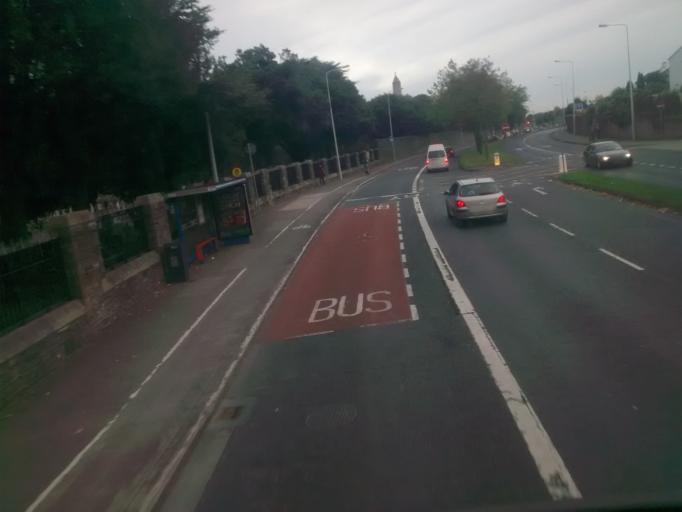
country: IE
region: Leinster
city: Cabra
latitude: 53.3725
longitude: -6.2829
